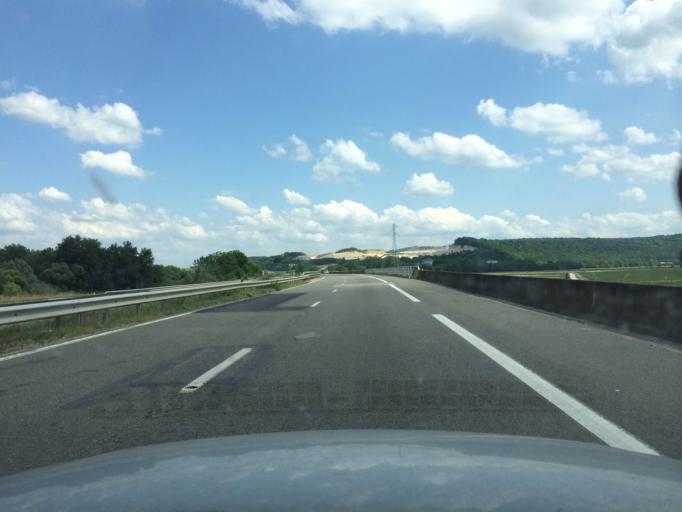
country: FR
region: Lorraine
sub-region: Departement de Meurthe-et-Moselle
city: Foug
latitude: 48.6867
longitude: 5.7095
